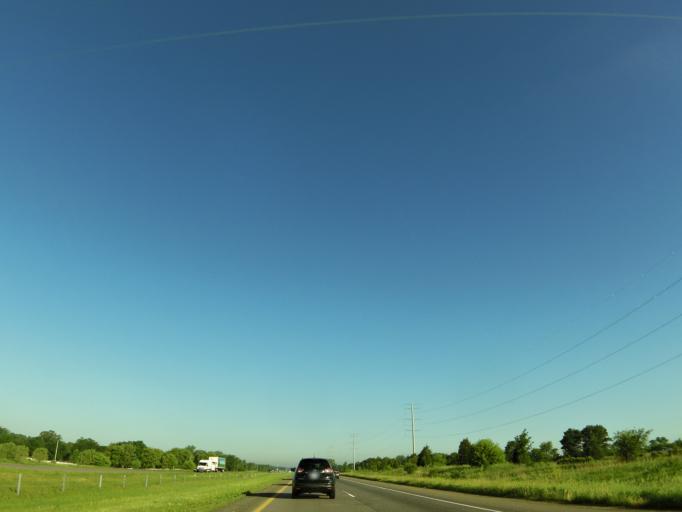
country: US
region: Minnesota
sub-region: Sherburne County
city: Becker
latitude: 45.3582
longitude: -93.9372
